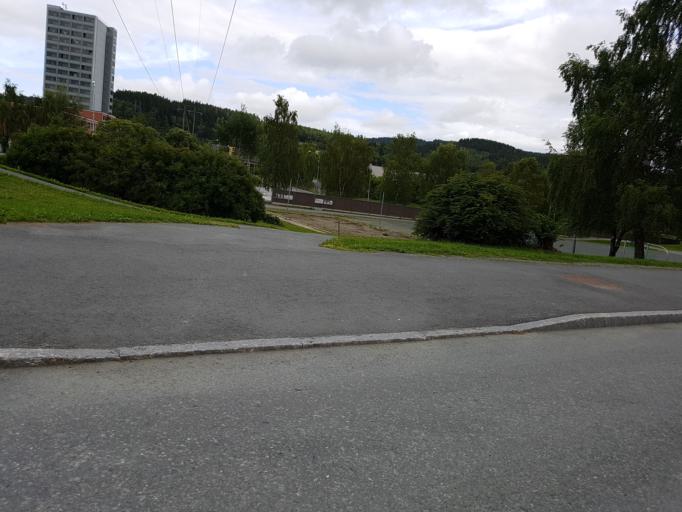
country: NO
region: Sor-Trondelag
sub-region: Trondheim
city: Trondheim
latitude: 63.3906
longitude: 10.4260
